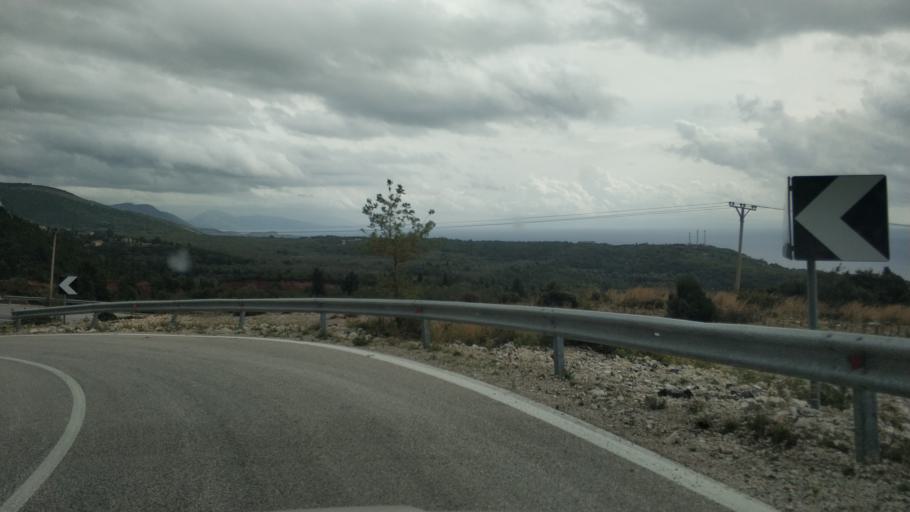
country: AL
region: Vlore
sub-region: Rrethi i Vlores
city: Vranisht
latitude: 40.1438
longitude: 19.6807
